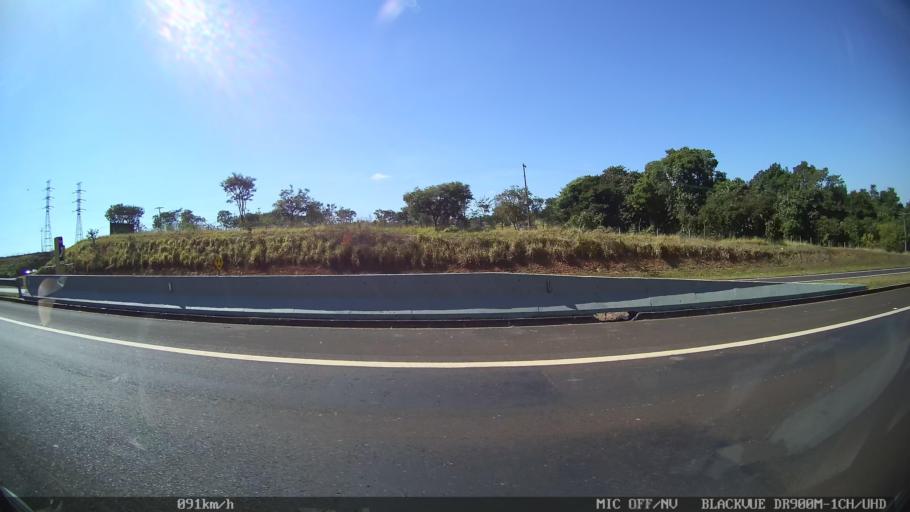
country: BR
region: Sao Paulo
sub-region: Franca
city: Franca
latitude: -20.4797
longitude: -47.4108
